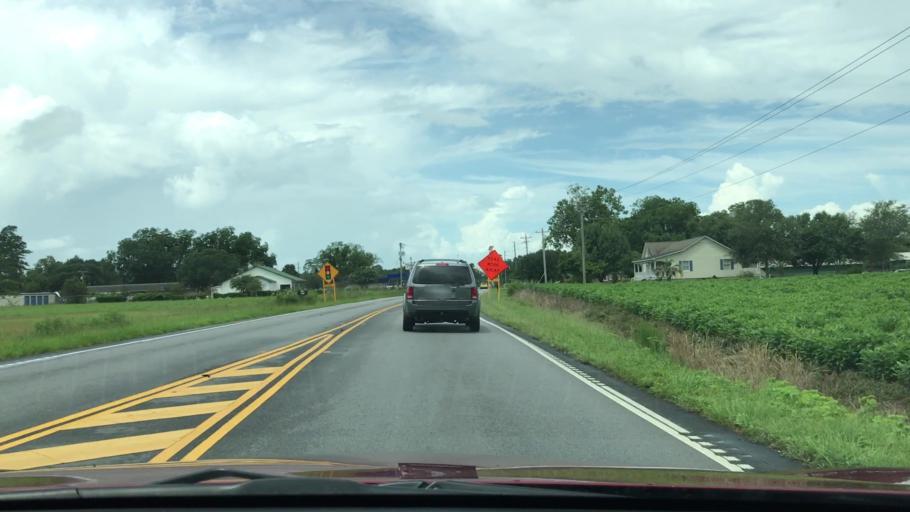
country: US
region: South Carolina
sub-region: Horry County
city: Loris
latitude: 33.9048
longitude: -78.8376
